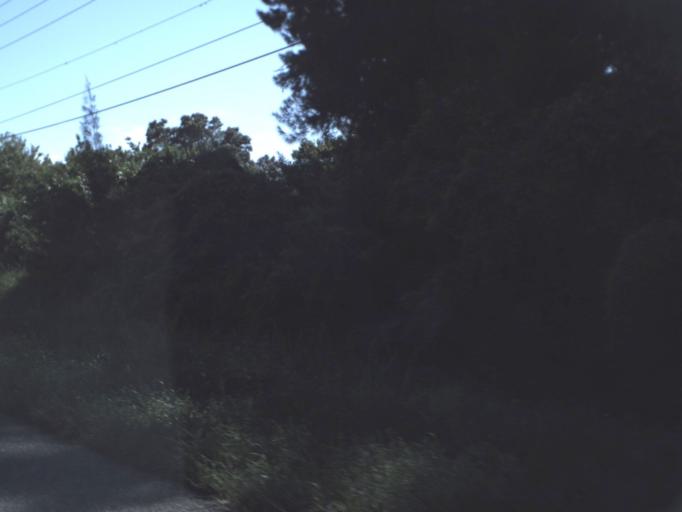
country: US
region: Florida
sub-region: Manatee County
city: Memphis
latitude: 27.5517
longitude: -82.5647
